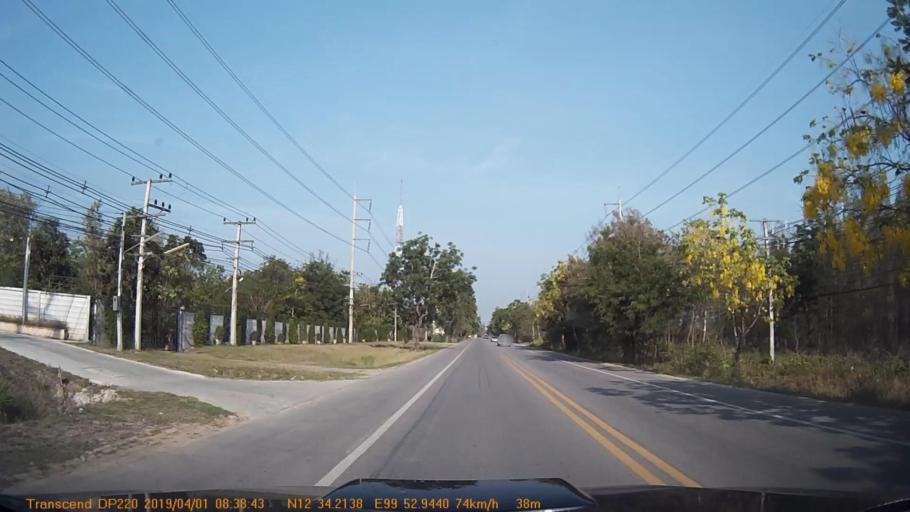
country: TH
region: Prachuap Khiri Khan
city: Hua Hin
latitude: 12.5703
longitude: 99.8823
